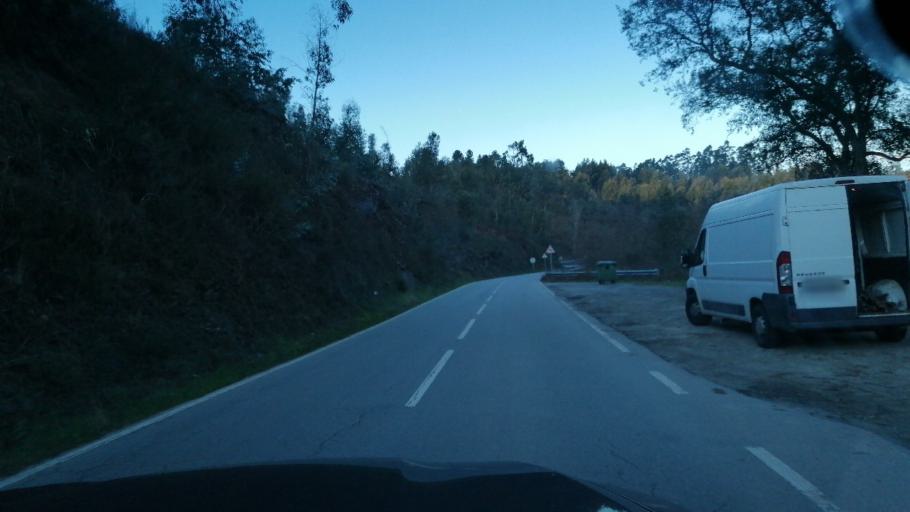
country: PT
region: Vila Real
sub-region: Mondim de Basto
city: Mondim de Basto
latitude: 41.4482
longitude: -7.9637
